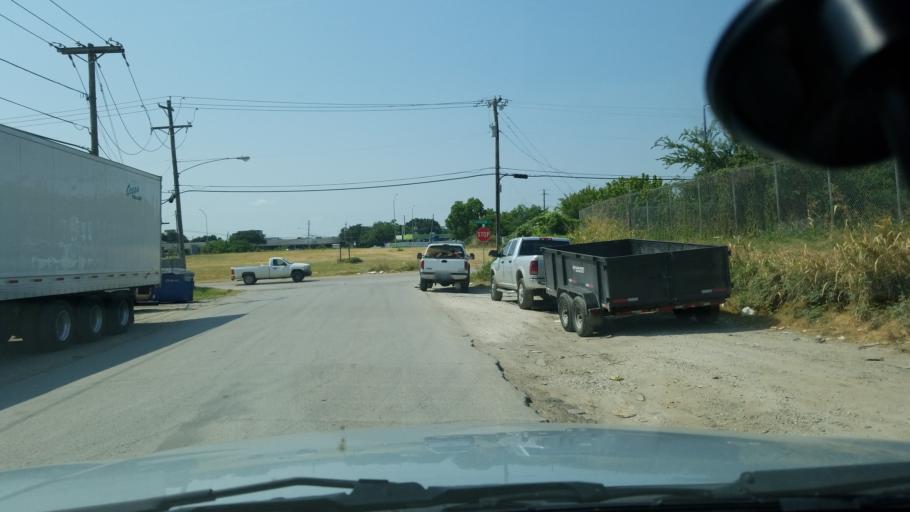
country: US
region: Texas
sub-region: Dallas County
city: Farmers Branch
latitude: 32.8671
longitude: -96.9024
